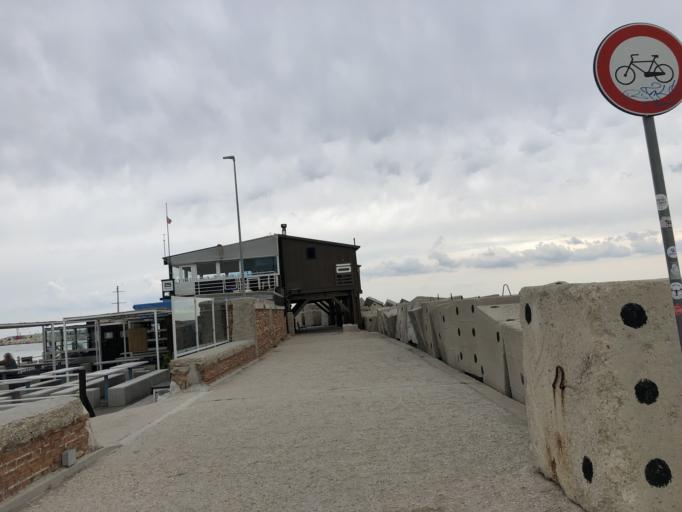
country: IT
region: The Marches
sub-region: Provincia di Pesaro e Urbino
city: Pesaro
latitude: 43.9245
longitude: 12.9069
